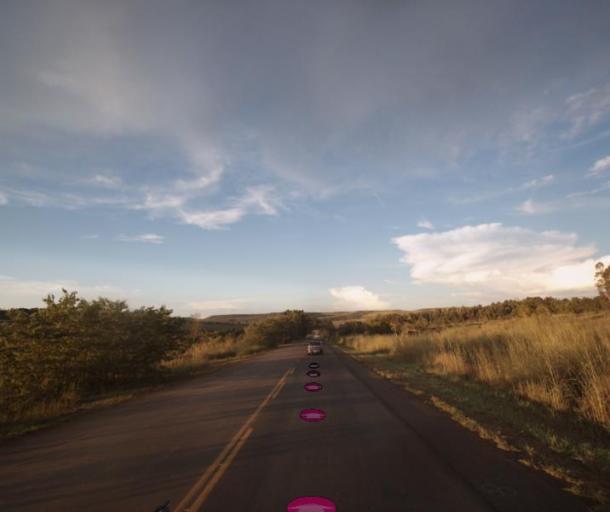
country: BR
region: Goias
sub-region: Anapolis
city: Anapolis
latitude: -16.1693
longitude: -48.8978
